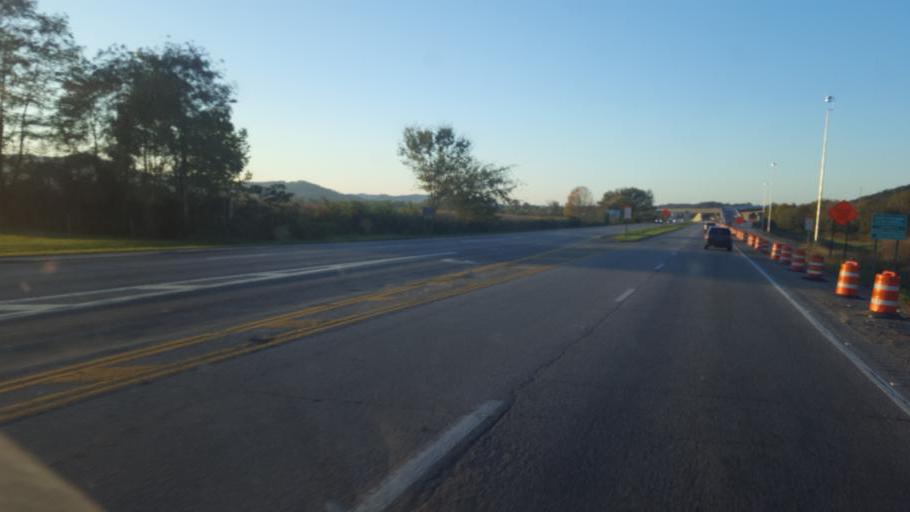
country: US
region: Ohio
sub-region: Scioto County
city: Lucasville
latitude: 38.8855
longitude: -82.9970
